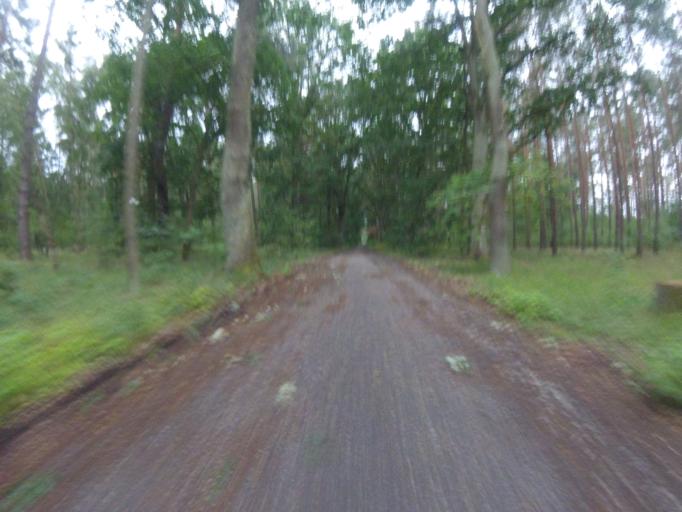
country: DE
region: Brandenburg
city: Bestensee
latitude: 52.2212
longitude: 13.7070
